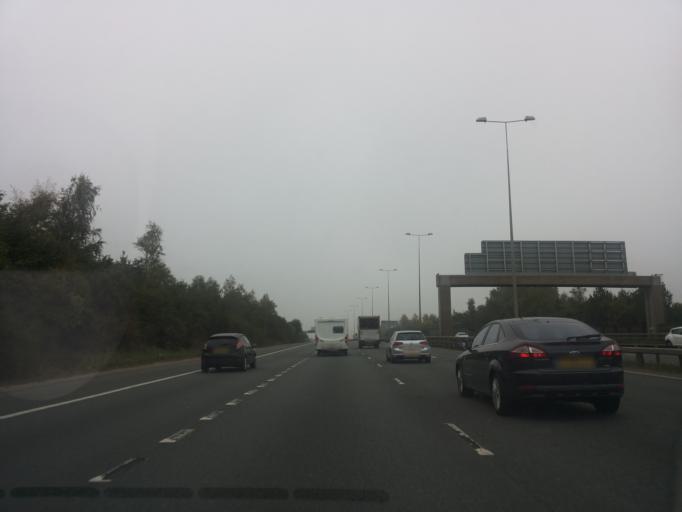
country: GB
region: England
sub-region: Borough of Tameside
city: Droylsden
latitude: 53.4723
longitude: -2.1326
